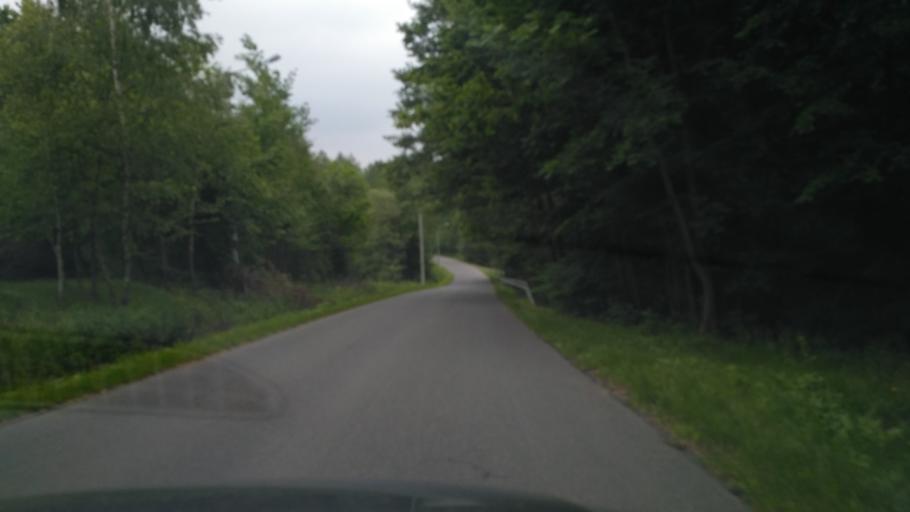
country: PL
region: Subcarpathian Voivodeship
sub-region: Powiat ropczycko-sedziszowski
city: Zagorzyce
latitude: 49.9937
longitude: 21.6936
